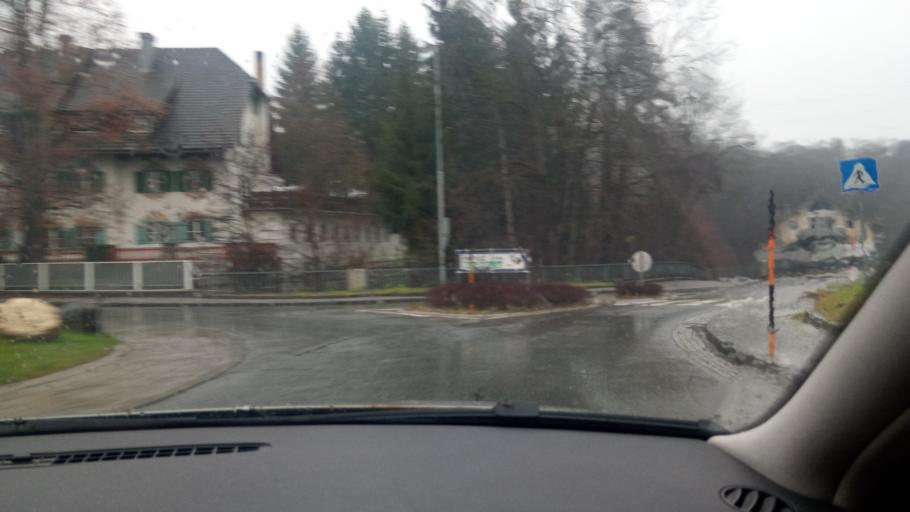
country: AT
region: Carinthia
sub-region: Politischer Bezirk Klagenfurt Land
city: Keutschach am See
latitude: 46.5921
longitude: 14.1696
